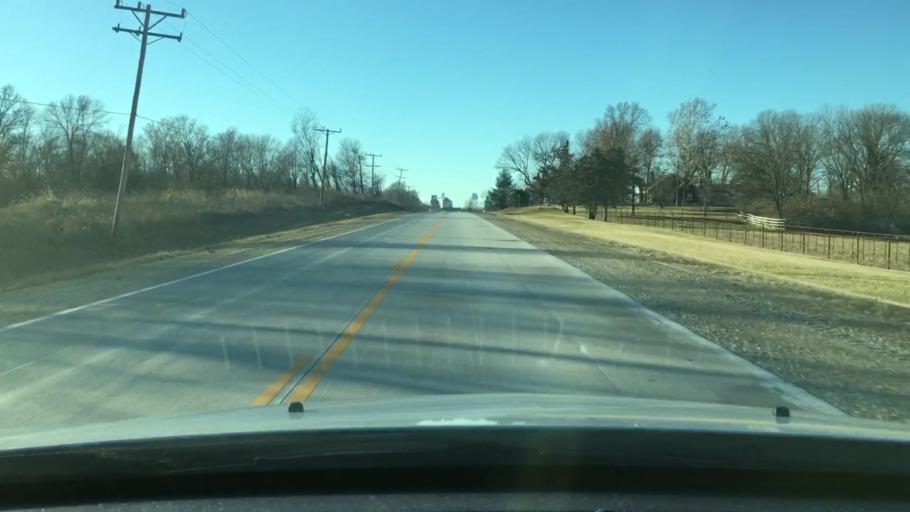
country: US
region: Missouri
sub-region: Boone County
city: Centralia
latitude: 39.2087
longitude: -92.1093
